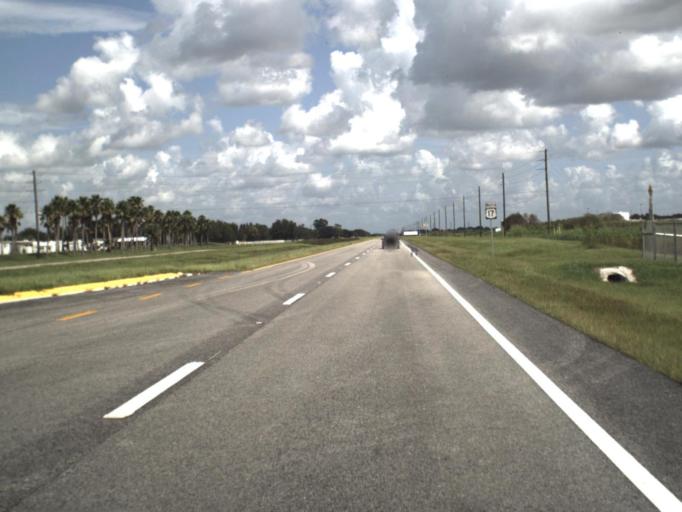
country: US
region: Florida
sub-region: Charlotte County
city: Harbour Heights
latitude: 27.0374
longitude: -81.9583
